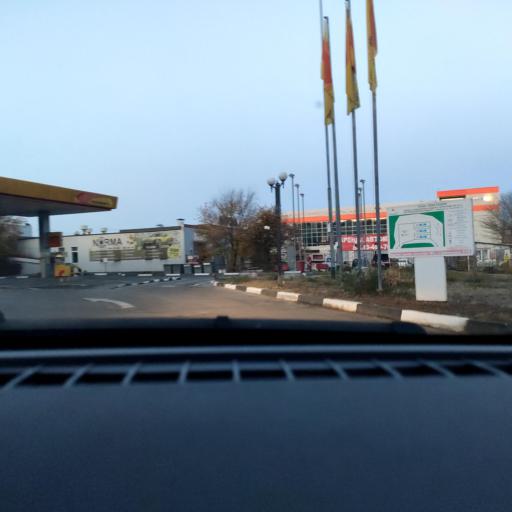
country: RU
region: Voronezj
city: Somovo
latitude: 51.7044
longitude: 39.2903
